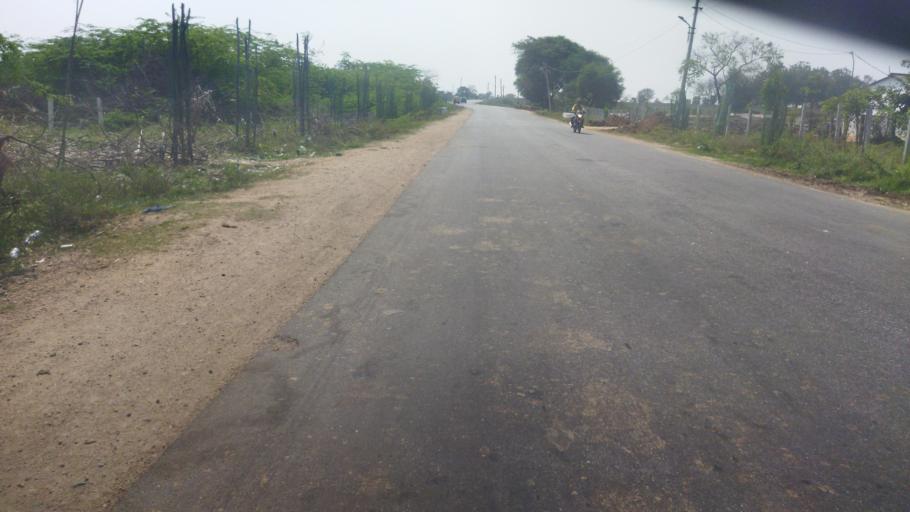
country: IN
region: Telangana
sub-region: Nalgonda
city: Nalgonda
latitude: 17.0859
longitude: 79.2846
